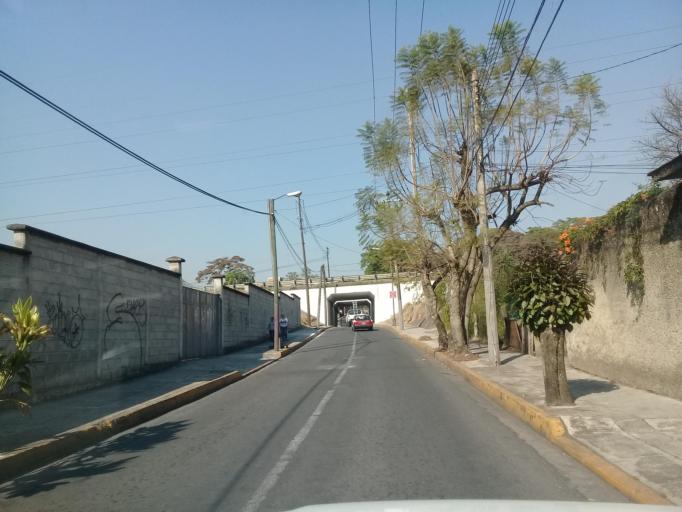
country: MX
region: Veracruz
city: Ixtac Zoquitlan
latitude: 18.8532
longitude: -97.0687
